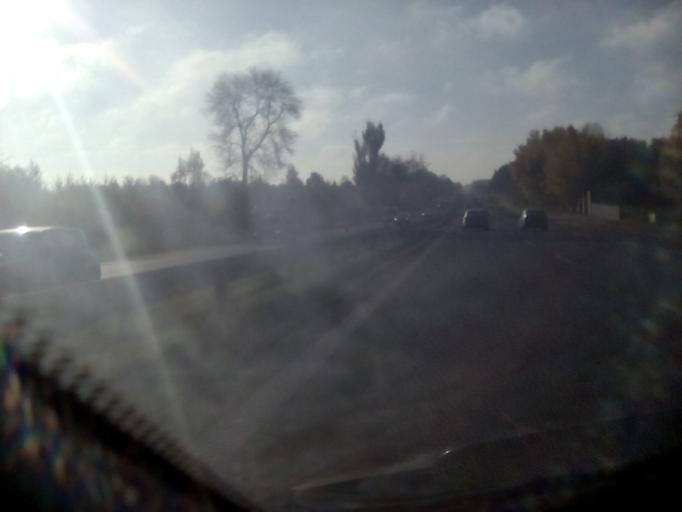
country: PL
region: Masovian Voivodeship
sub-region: Powiat piaseczynski
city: Tarczyn
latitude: 51.9269
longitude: 20.8505
